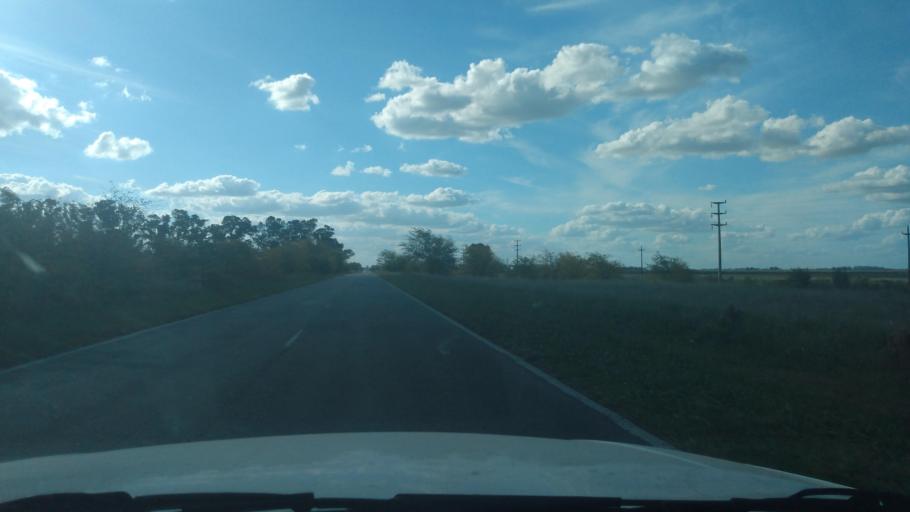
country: AR
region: Buenos Aires
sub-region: Partido de Navarro
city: Navarro
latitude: -34.9259
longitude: -59.3259
